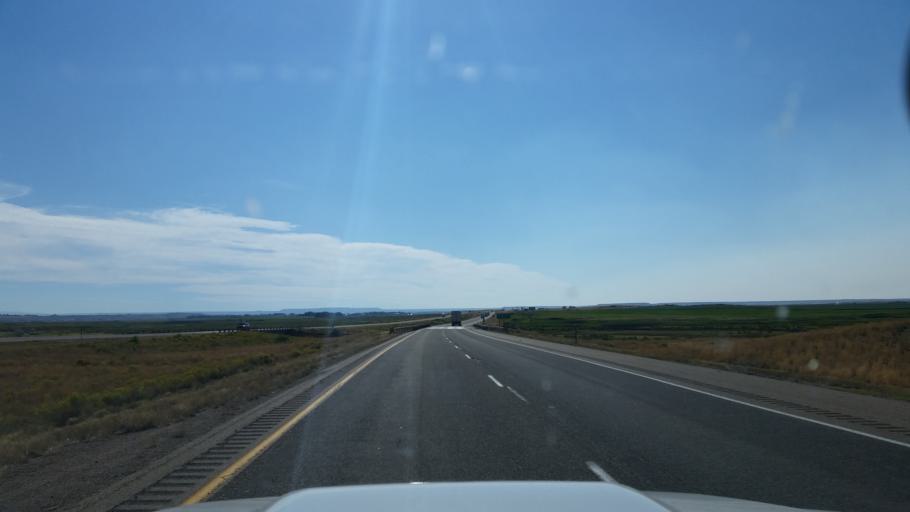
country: US
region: Wyoming
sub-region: Uinta County
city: Lyman
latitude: 41.3751
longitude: -110.2439
